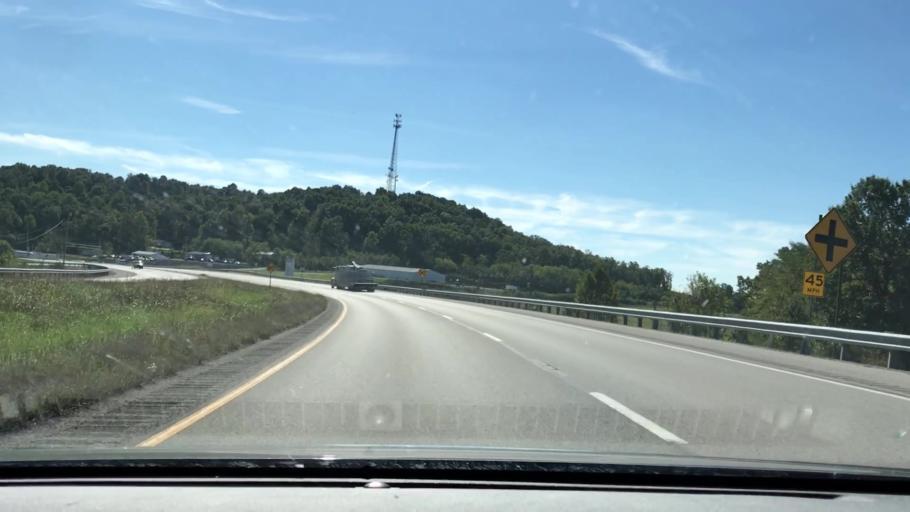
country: US
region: Kentucky
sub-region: Logan County
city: Russellville
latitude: 36.8373
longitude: -86.9178
